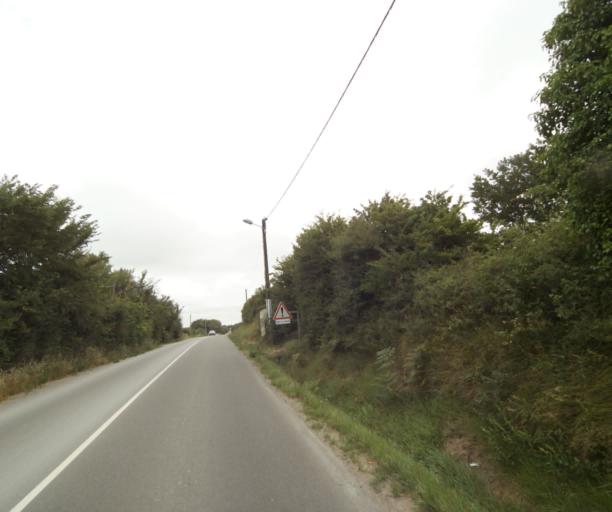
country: FR
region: Pays de la Loire
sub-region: Departement de la Vendee
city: Chateau-d'Olonne
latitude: 46.4833
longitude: -1.7144
